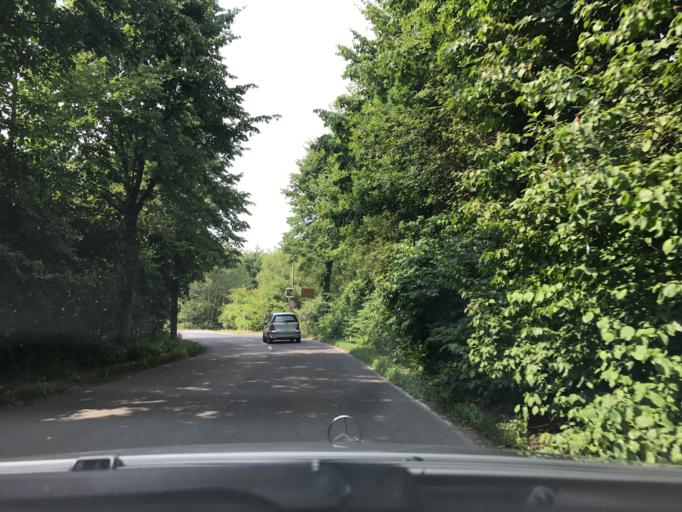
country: DE
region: North Rhine-Westphalia
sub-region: Regierungsbezirk Dusseldorf
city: Krefeld
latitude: 51.3815
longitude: 6.6067
